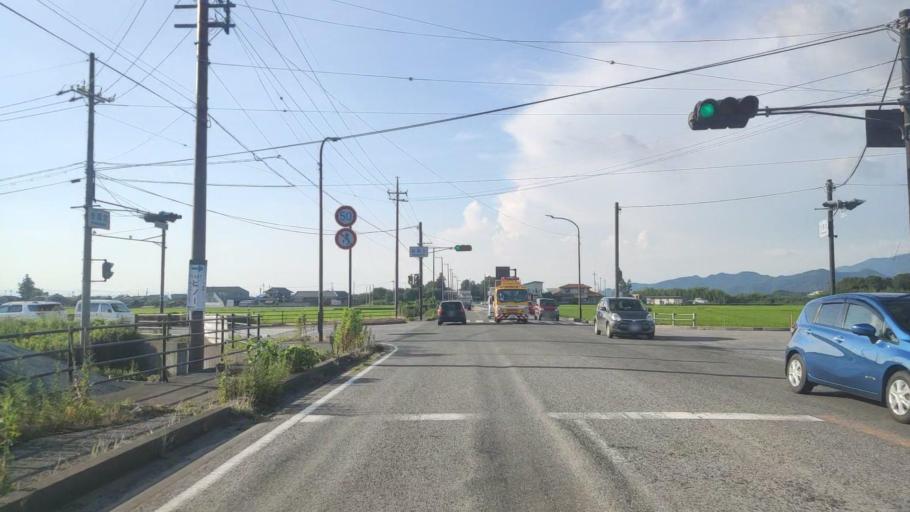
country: JP
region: Shiga Prefecture
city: Hikone
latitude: 35.2021
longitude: 136.2762
